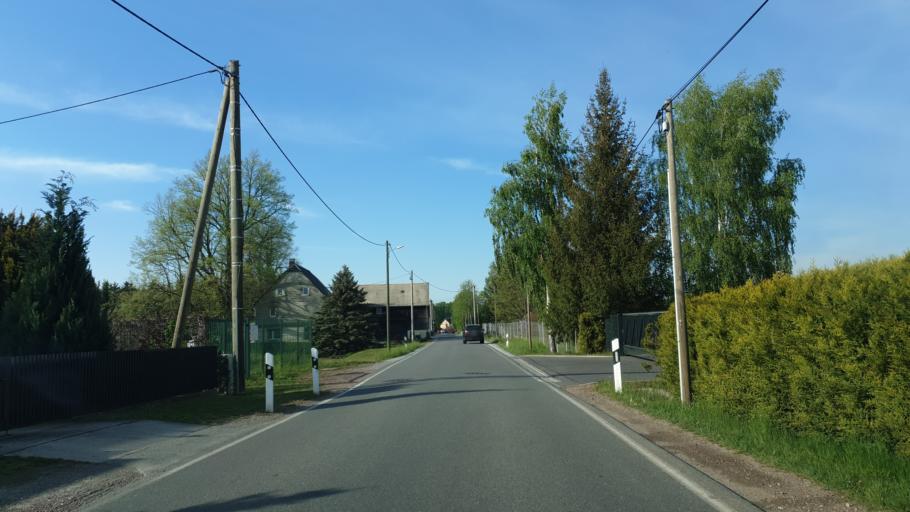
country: DE
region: Saxony
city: Jahnsdorf
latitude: 50.7583
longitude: 12.8604
